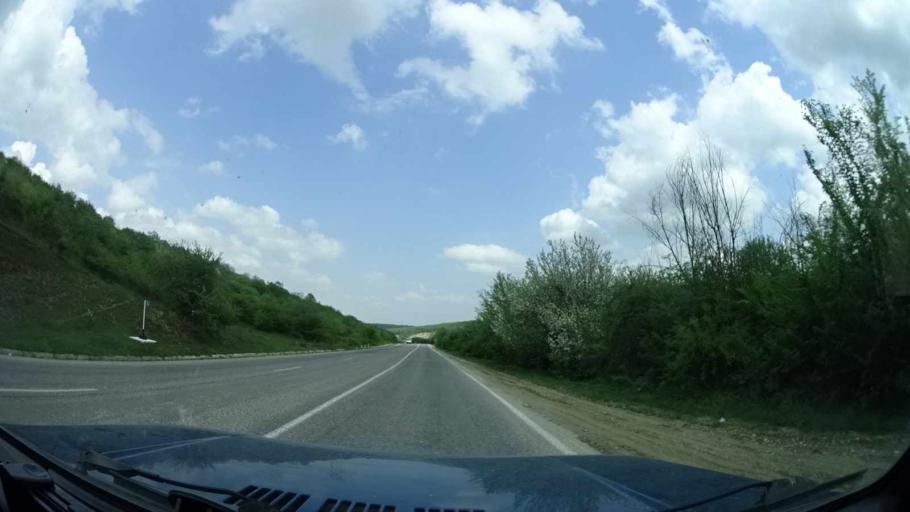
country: RU
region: Dagestan
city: Erpeli
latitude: 42.7940
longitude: 46.9963
